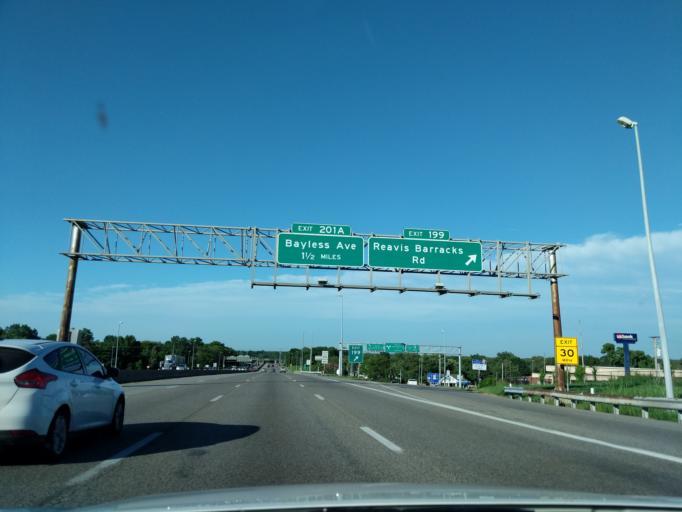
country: US
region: Missouri
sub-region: Saint Louis County
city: Saint George
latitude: 38.5313
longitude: -90.3131
